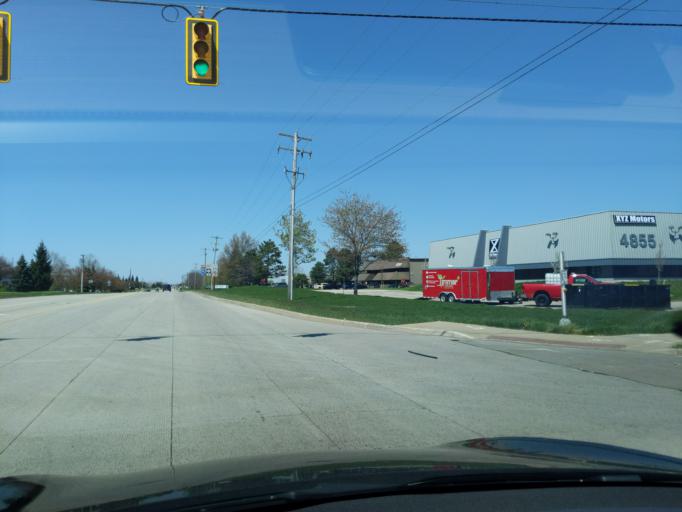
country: US
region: Michigan
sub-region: Kent County
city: Caledonia
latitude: 42.8690
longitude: -85.5463
